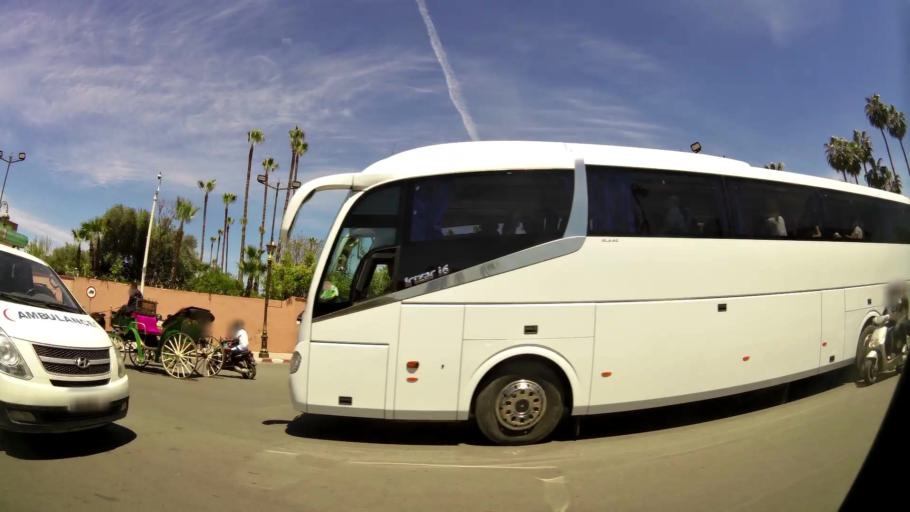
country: MA
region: Marrakech-Tensift-Al Haouz
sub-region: Marrakech
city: Marrakesh
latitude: 31.6264
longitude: -7.9954
